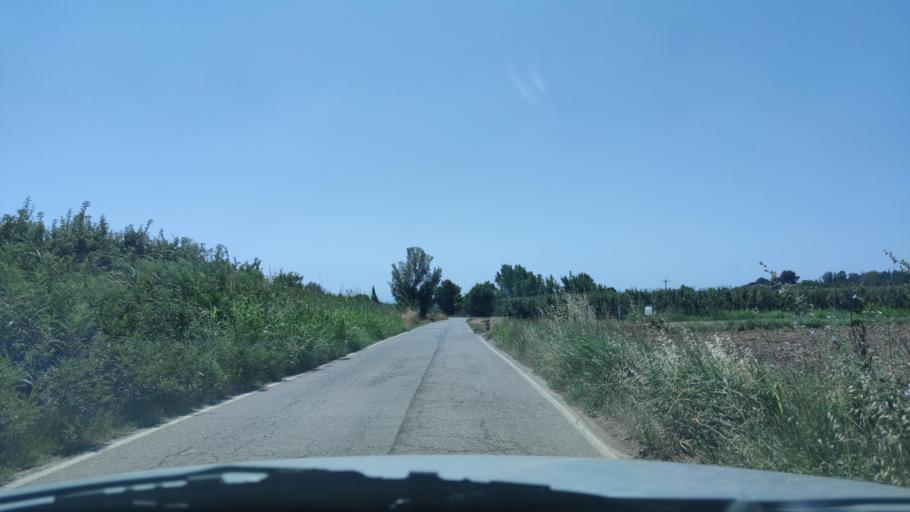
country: ES
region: Catalonia
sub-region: Provincia de Lleida
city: Torrefarrera
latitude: 41.6522
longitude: 0.5978
